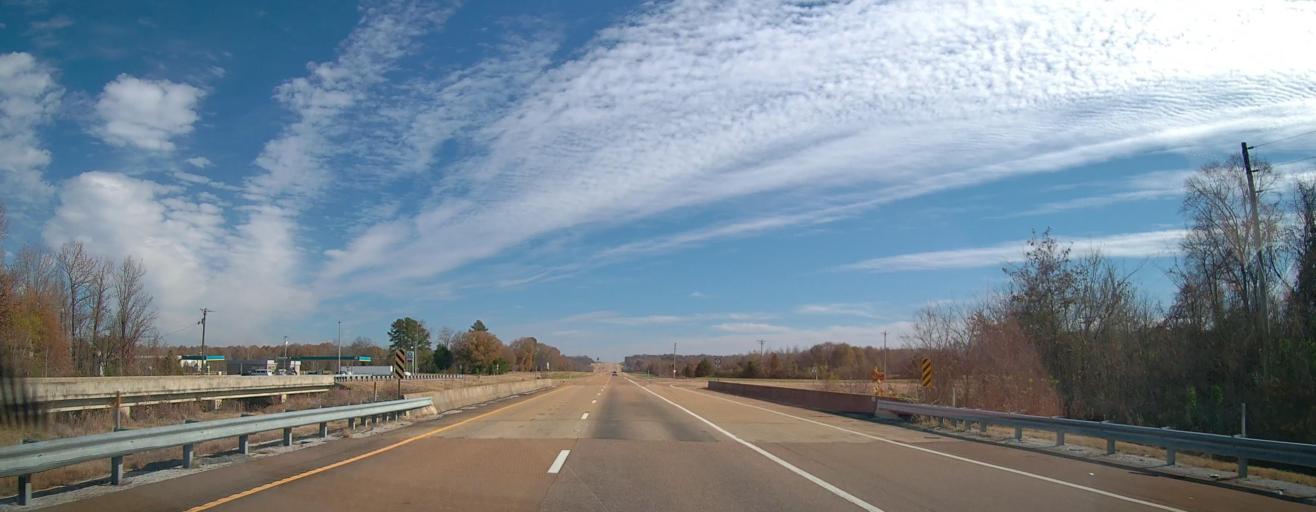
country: US
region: Mississippi
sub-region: Benton County
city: Ashland
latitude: 34.9462
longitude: -89.2126
